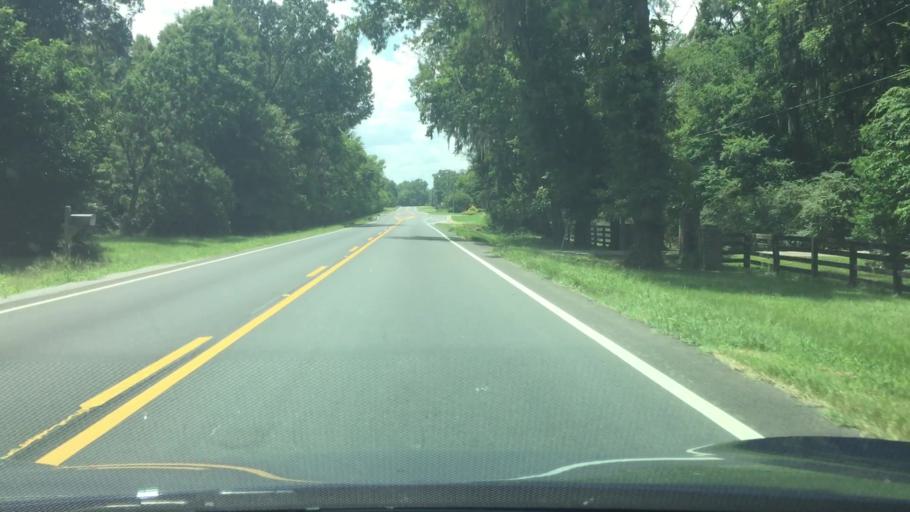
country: US
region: Alabama
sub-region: Montgomery County
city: Pike Road
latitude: 32.3260
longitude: -86.0945
